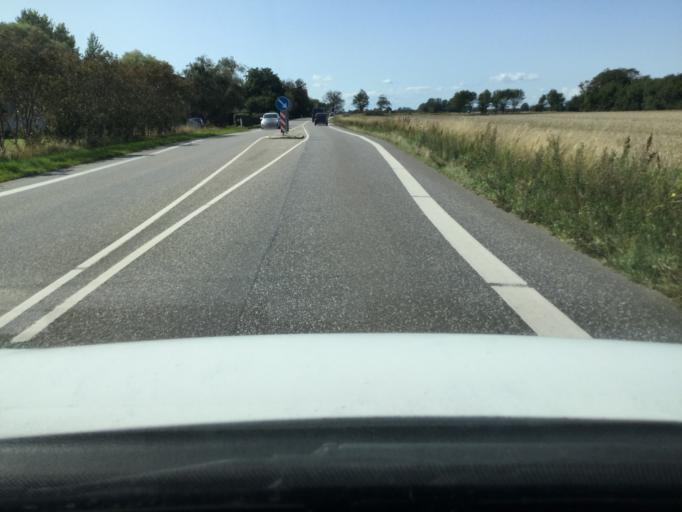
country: DK
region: Zealand
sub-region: Lolland Kommune
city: Nakskov
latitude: 54.8046
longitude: 11.2364
